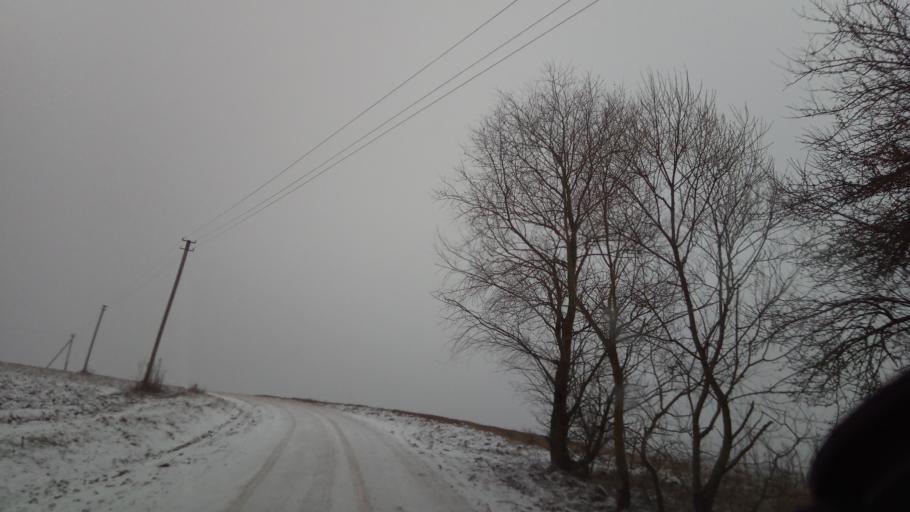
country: LT
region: Vilnius County
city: Ukmerge
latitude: 55.3430
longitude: 24.9573
